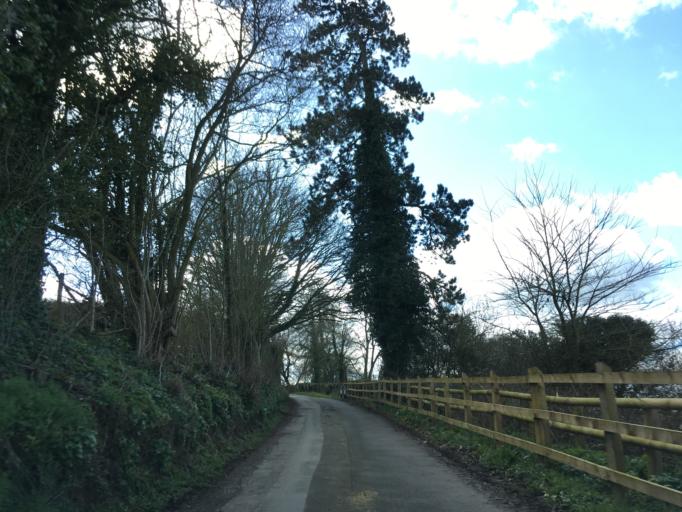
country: GB
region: England
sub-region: South Gloucestershire
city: Horton
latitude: 51.5600
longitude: -2.3434
